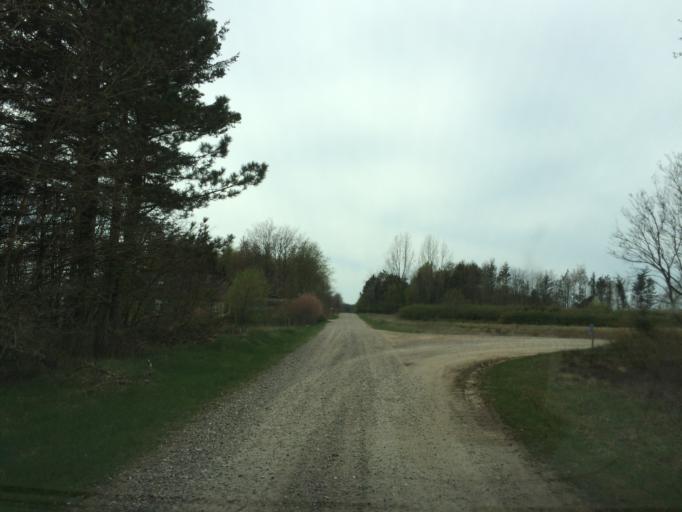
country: DK
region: Central Jutland
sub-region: Holstebro Kommune
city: Ulfborg
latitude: 56.2488
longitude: 8.4215
